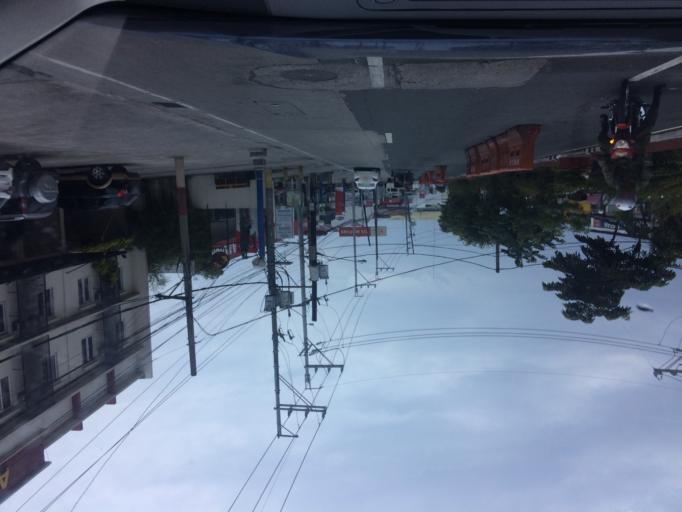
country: PH
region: Metro Manila
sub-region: Makati City
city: Makati City
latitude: 14.5283
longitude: 121.0049
